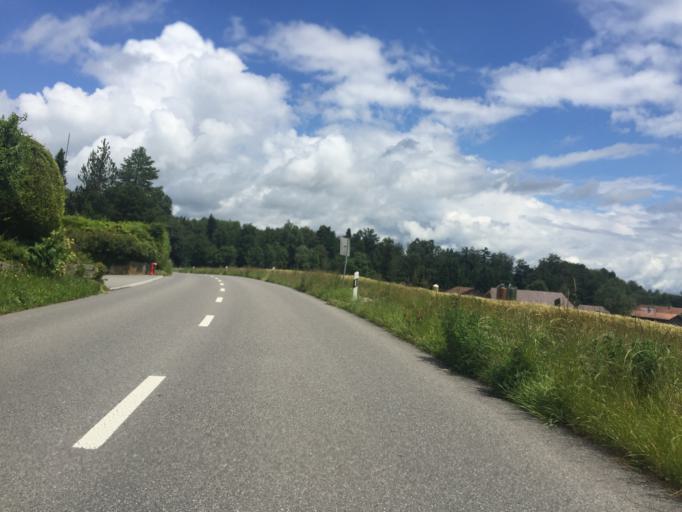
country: CH
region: Bern
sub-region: Bern-Mittelland District
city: Wohlen
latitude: 46.9794
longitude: 7.3683
